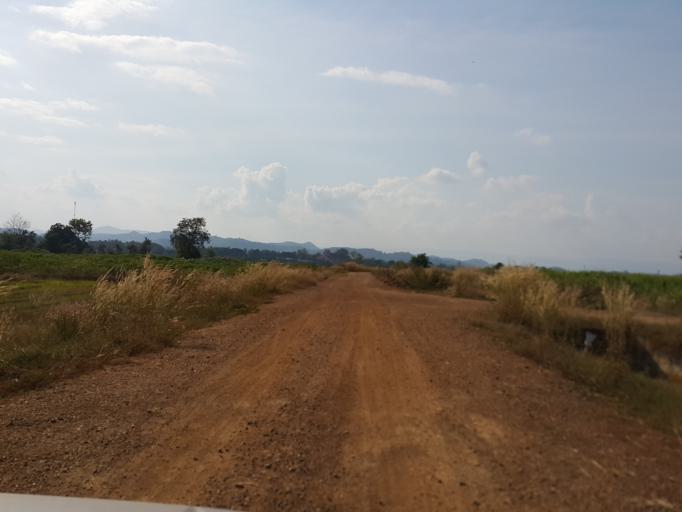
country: TH
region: Sukhothai
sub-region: Amphoe Si Satchanalai
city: Si Satchanalai
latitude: 17.4739
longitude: 99.6581
